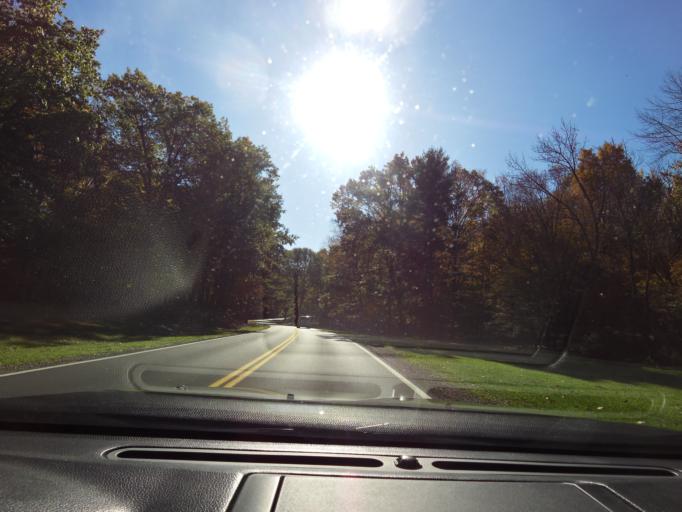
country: US
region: New York
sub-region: Wyoming County
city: Castile
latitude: 42.5966
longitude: -78.0287
